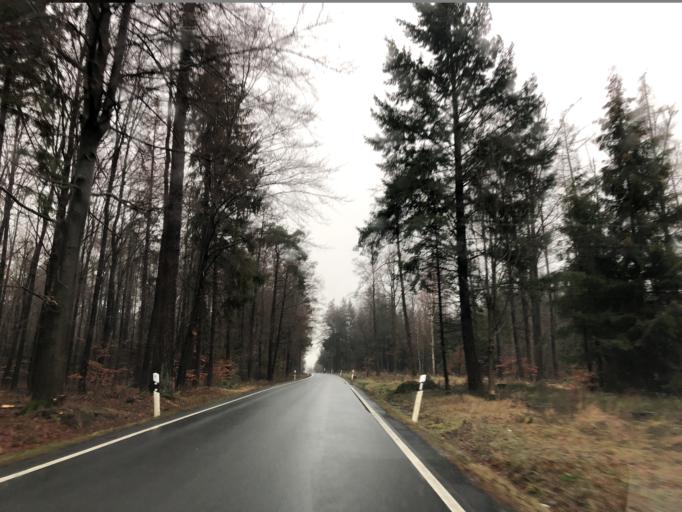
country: DE
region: Hesse
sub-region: Regierungsbezirk Darmstadt
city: Lutzelbach
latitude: 49.7295
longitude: 9.0848
